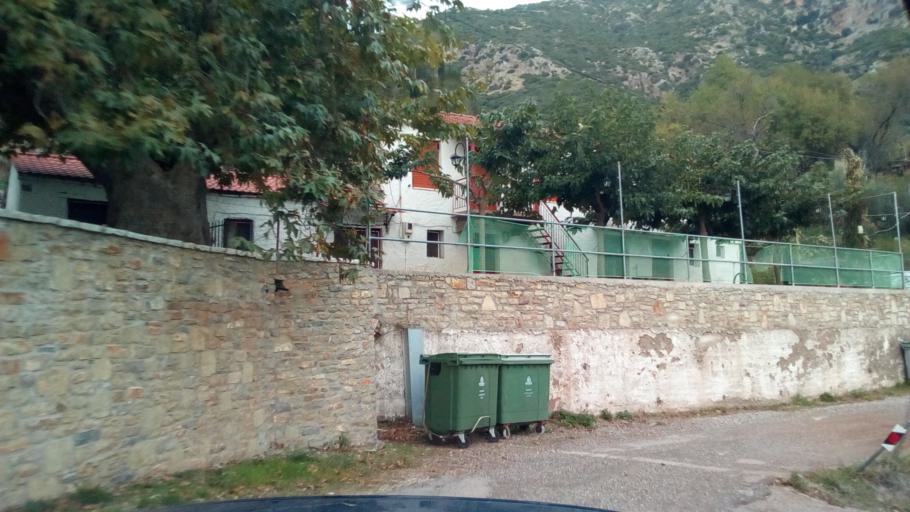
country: GR
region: West Greece
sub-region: Nomos Achaias
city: Kamarai
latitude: 38.4133
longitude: 22.0571
